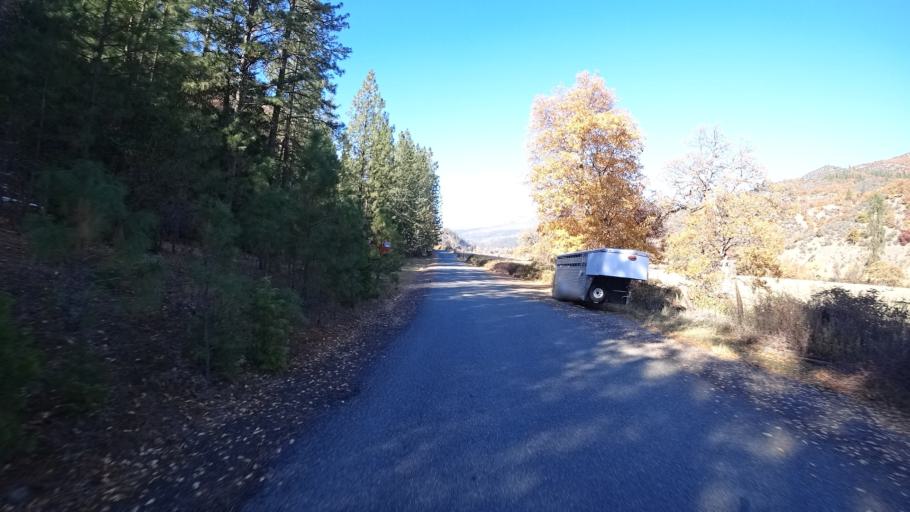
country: US
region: California
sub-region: Siskiyou County
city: Yreka
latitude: 41.8343
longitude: -122.8553
